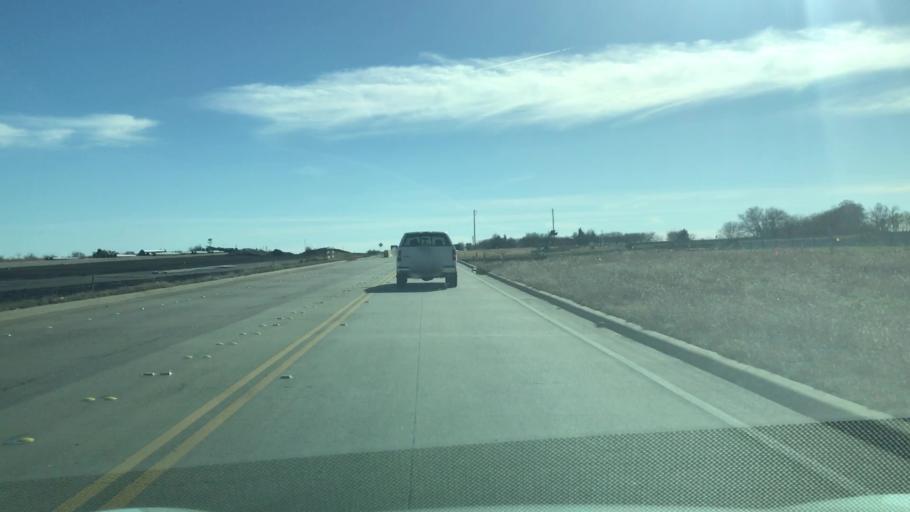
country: US
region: Texas
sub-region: Tarrant County
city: Mansfield
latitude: 32.5351
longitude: -97.0822
